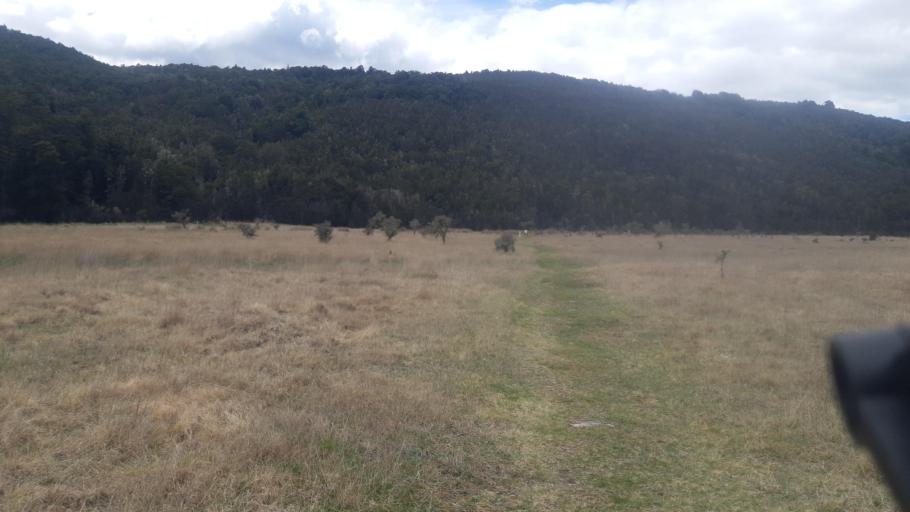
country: NZ
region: Tasman
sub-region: Tasman District
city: Wakefield
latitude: -41.7825
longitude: 172.8198
